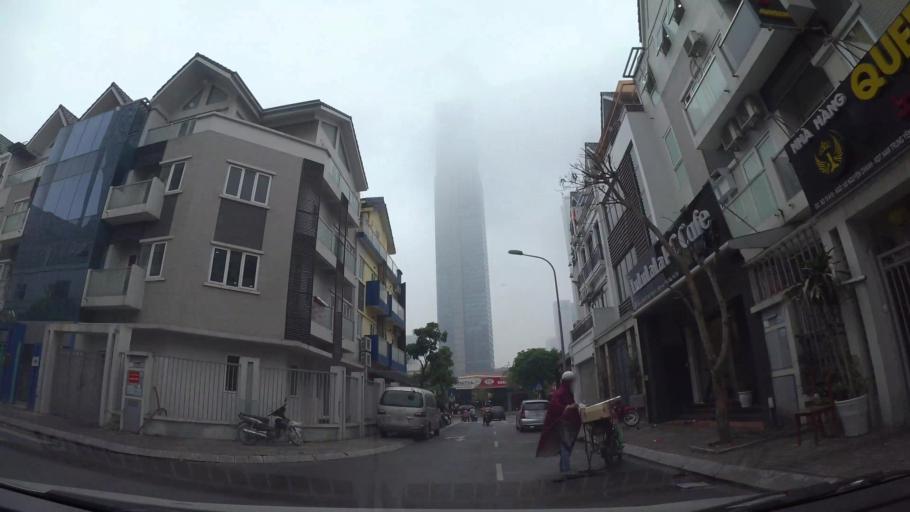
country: VN
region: Ha Noi
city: Cau Giay
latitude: 21.0192
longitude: 105.7872
